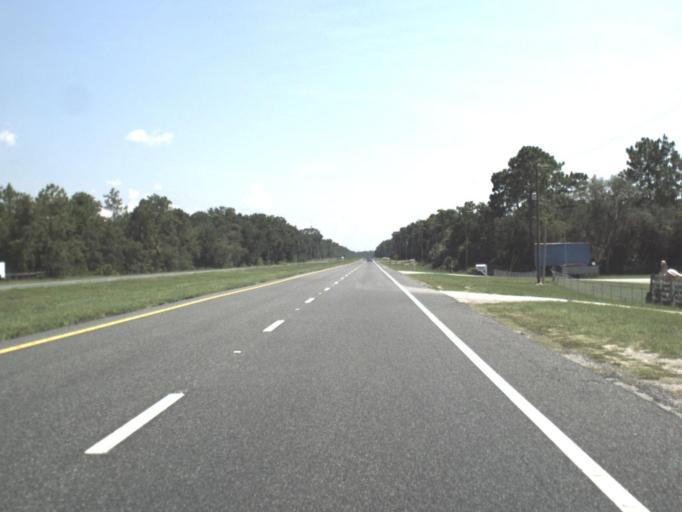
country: US
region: Florida
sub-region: Levy County
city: Inglis
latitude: 29.1190
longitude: -82.6367
